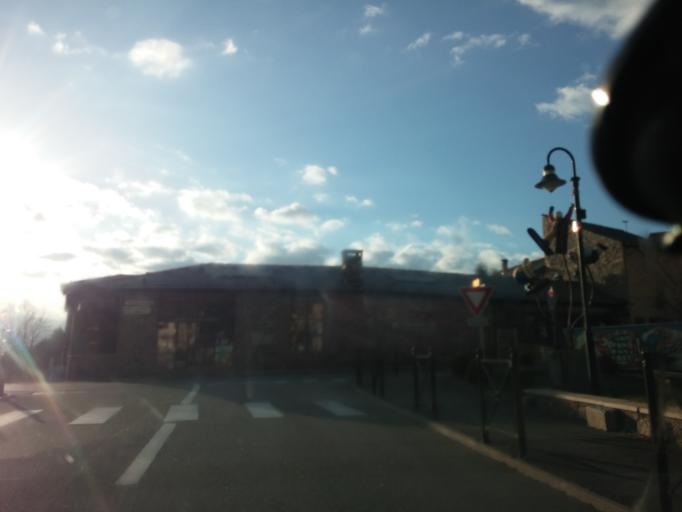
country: ES
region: Catalonia
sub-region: Provincia de Girona
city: Llivia
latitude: 42.4581
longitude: 2.0388
